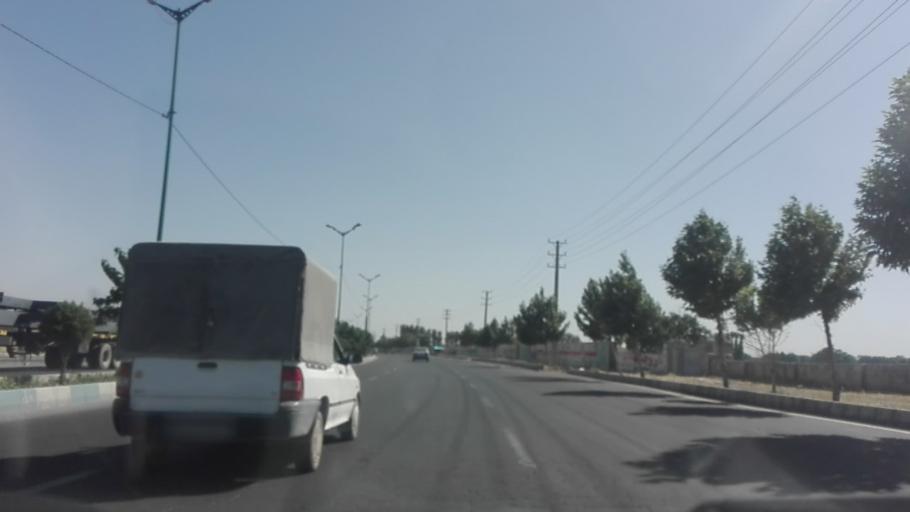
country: IR
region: Tehran
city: Shahriar
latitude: 35.6314
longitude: 51.0568
